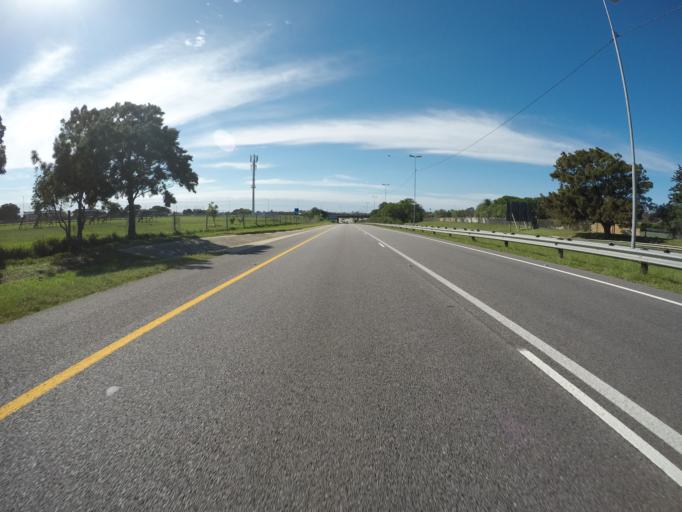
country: ZA
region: Eastern Cape
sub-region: Nelson Mandela Bay Metropolitan Municipality
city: Port Elizabeth
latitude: -33.9470
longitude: 25.5237
